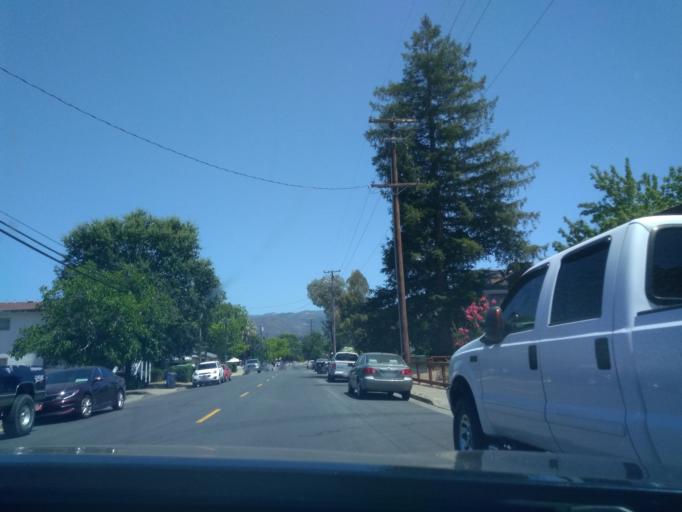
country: US
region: California
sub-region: Mendocino County
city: Ukiah
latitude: 39.1374
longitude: -123.2084
